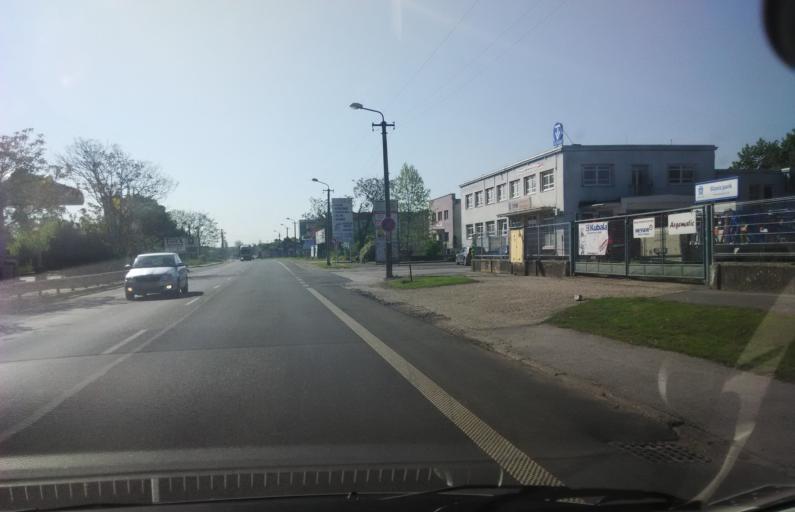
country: SK
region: Nitriansky
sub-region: Okres Nitra
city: Nitra
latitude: 48.2805
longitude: 18.0924
